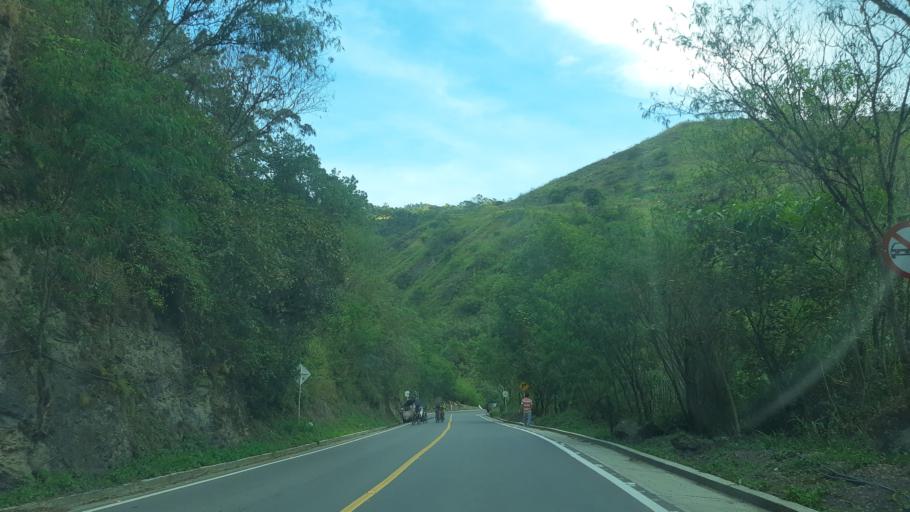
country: CO
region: Boyaca
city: Somondoco
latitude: 5.0094
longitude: -73.4364
